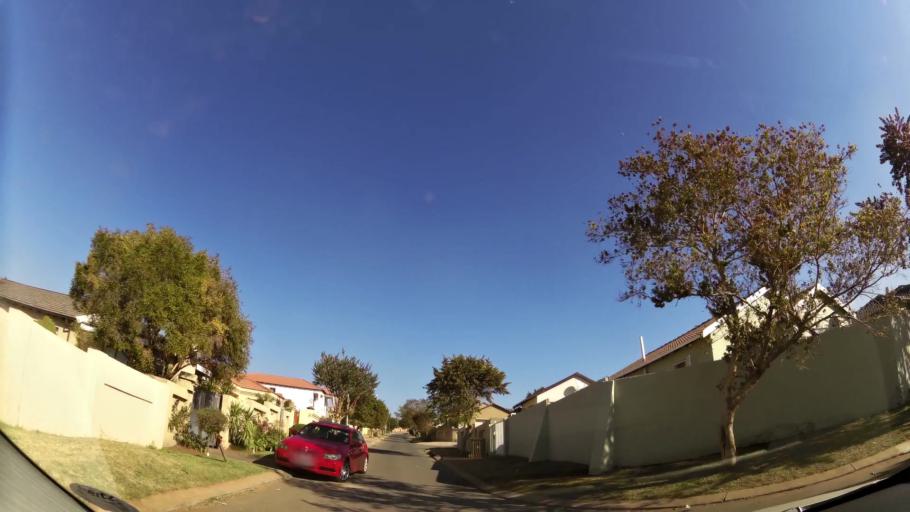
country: ZA
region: Gauteng
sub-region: City of Johannesburg Metropolitan Municipality
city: Roodepoort
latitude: -26.1573
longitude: 27.8352
